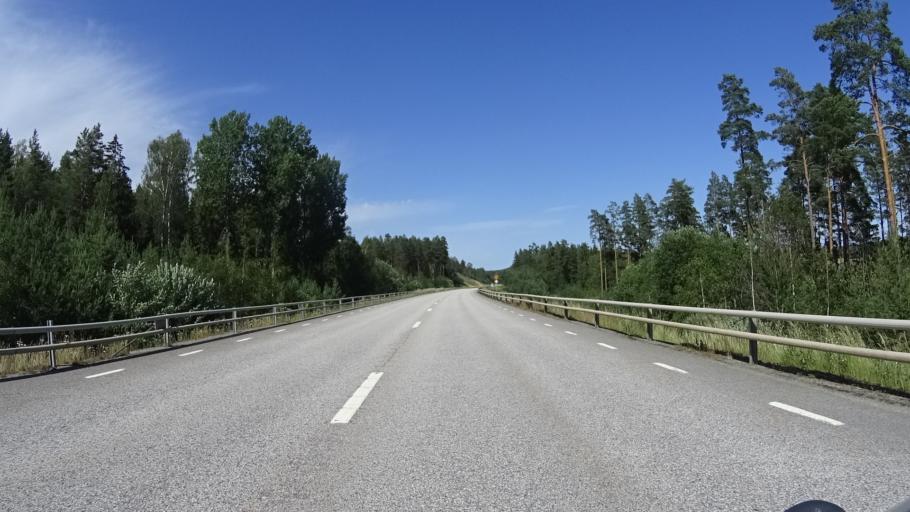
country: SE
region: Kalmar
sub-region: Vasterviks Kommun
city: Gamleby
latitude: 57.9281
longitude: 16.3762
